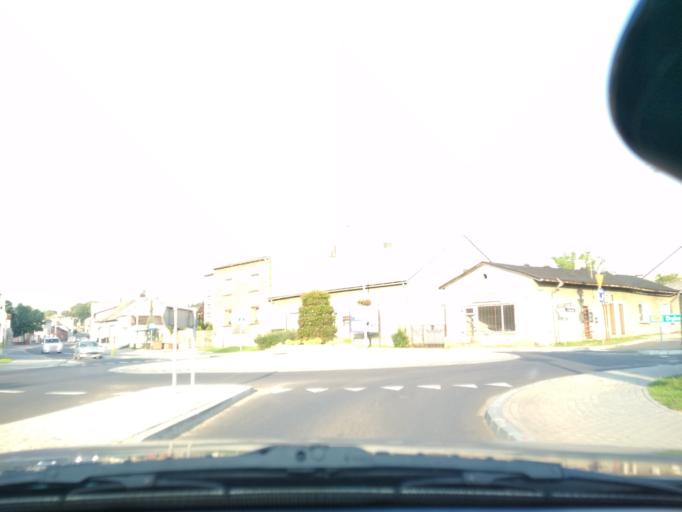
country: PL
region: Silesian Voivodeship
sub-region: Powiat zawiercianski
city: Ogrodzieniec
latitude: 50.4513
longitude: 19.5187
